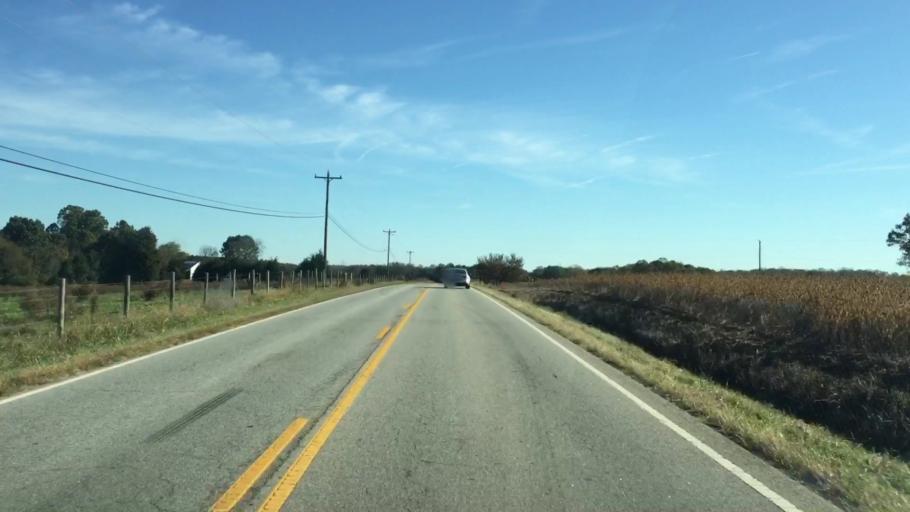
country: US
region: North Carolina
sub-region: Rowan County
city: Landis
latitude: 35.6382
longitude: -80.6634
